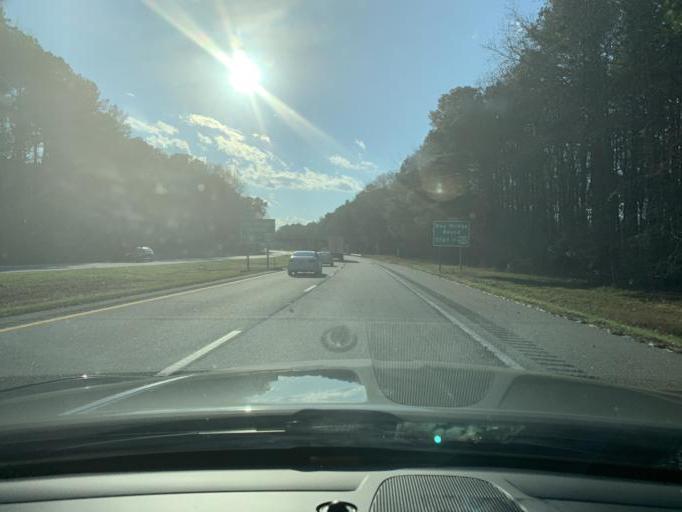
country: US
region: Maryland
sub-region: Queen Anne's County
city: Grasonville
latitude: 38.9827
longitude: -76.1662
